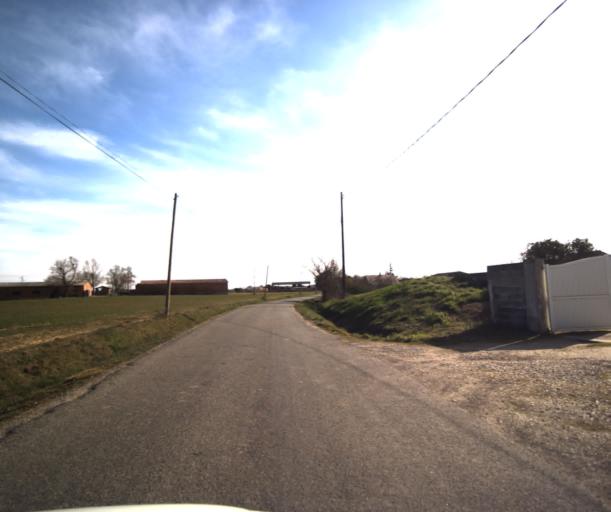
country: FR
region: Midi-Pyrenees
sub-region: Departement du Tarn-et-Garonne
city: Campsas
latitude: 43.9186
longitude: 1.3275
